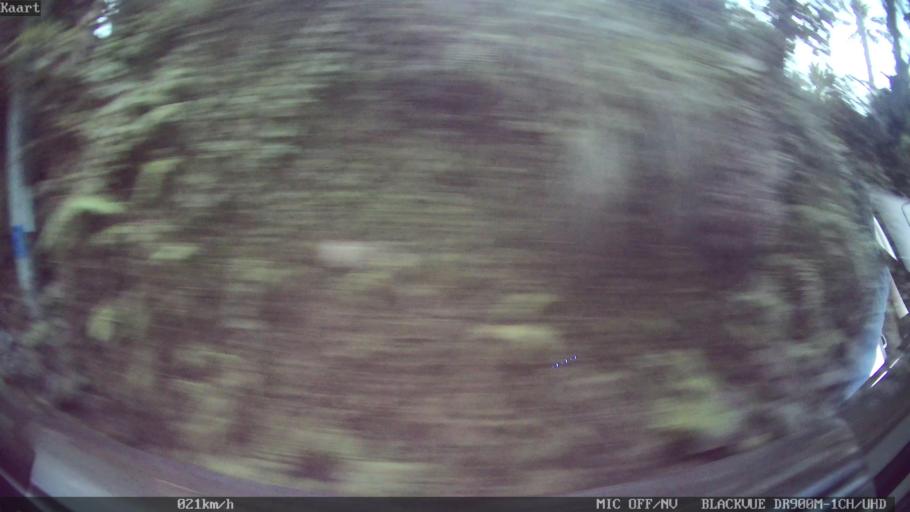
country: ID
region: Bali
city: Peneng
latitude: -8.3430
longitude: 115.1850
